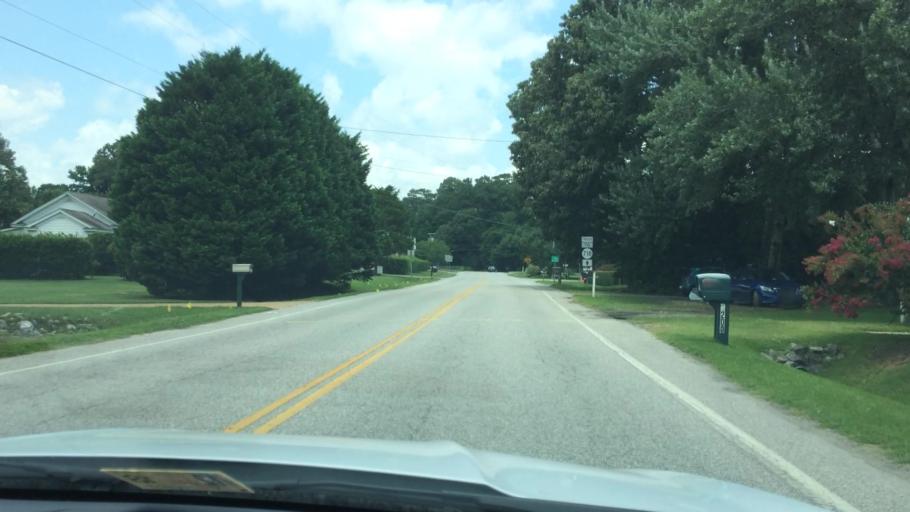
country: US
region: Virginia
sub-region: York County
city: Yorktown
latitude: 37.1935
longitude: -76.4816
